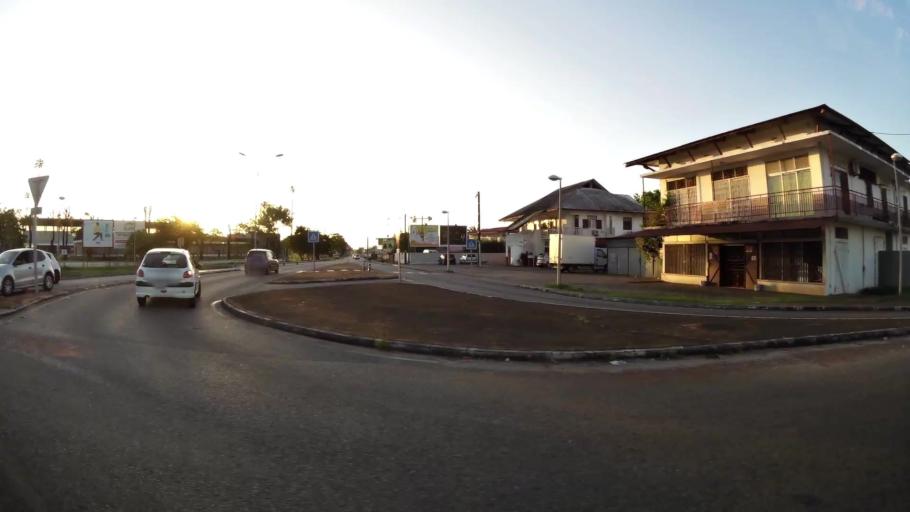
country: GF
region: Guyane
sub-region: Guyane
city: Cayenne
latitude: 4.9333
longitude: -52.3097
